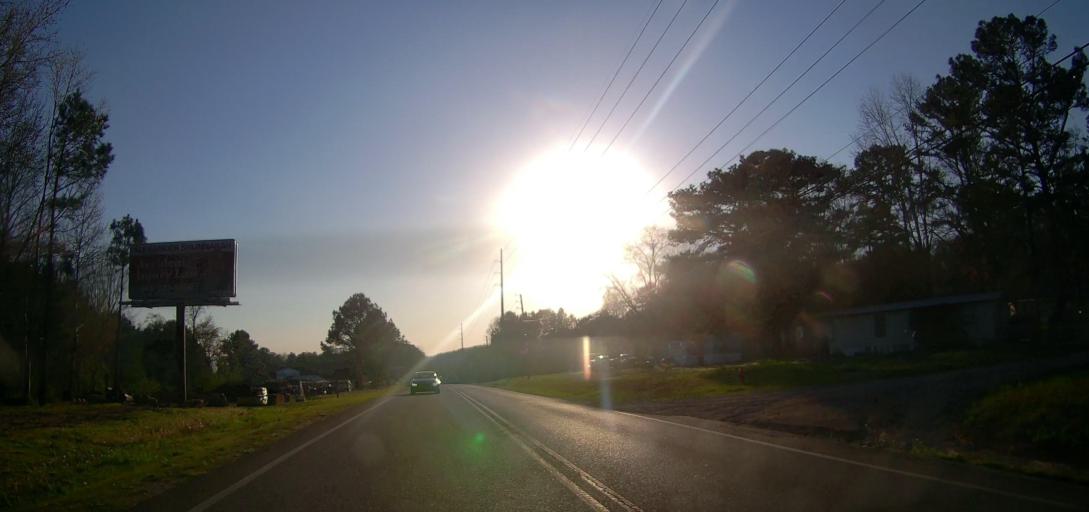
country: US
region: Alabama
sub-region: Shelby County
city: Indian Springs Village
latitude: 33.3176
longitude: -86.7179
